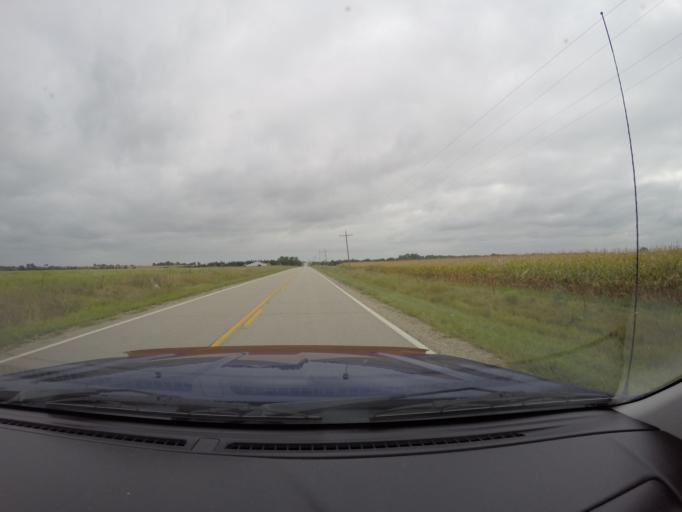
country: US
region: Kansas
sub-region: Morris County
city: Council Grove
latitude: 38.8353
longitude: -96.5941
